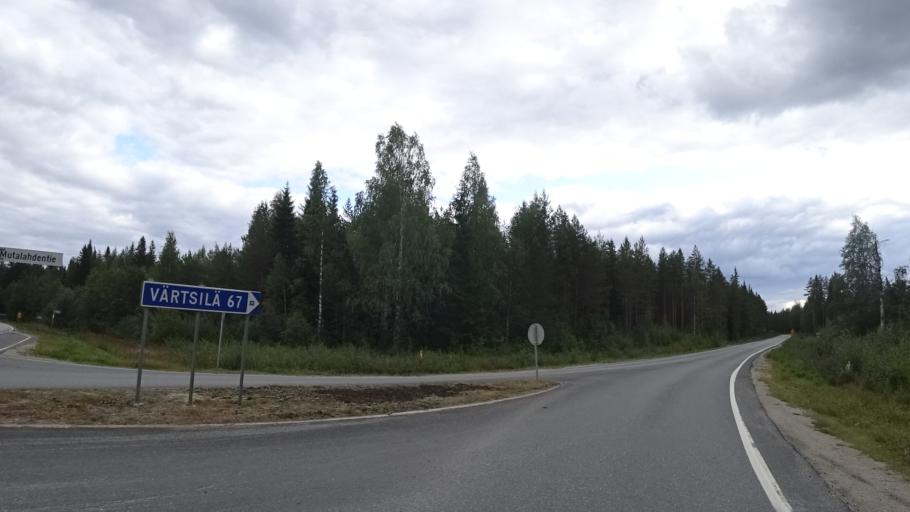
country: FI
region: North Karelia
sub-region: Joensuu
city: Ilomantsi
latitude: 62.6492
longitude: 30.9786
